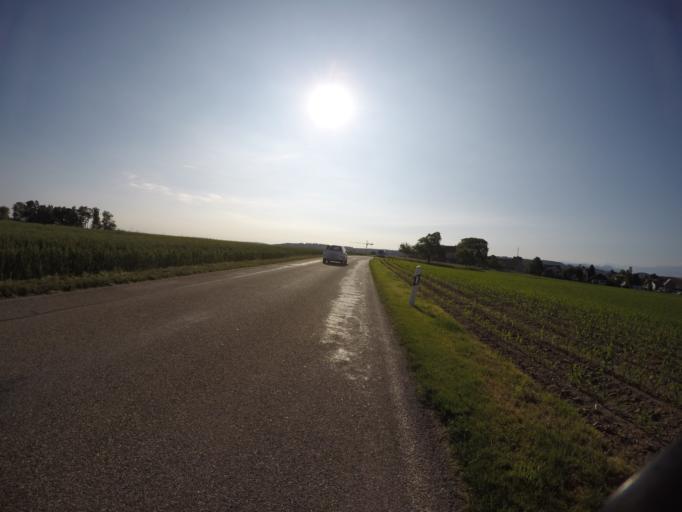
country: CH
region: Zurich
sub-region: Bezirk Winterthur
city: Brutten
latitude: 47.4582
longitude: 8.6873
